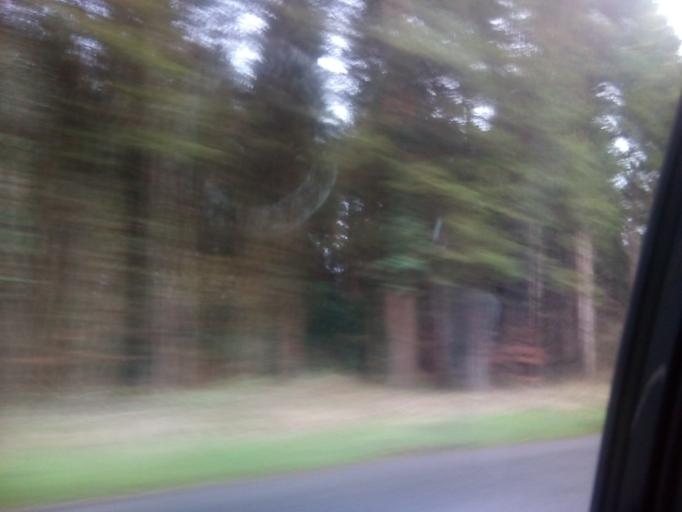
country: IE
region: Leinster
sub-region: Laois
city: Abbeyleix
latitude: 52.8921
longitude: -7.3627
